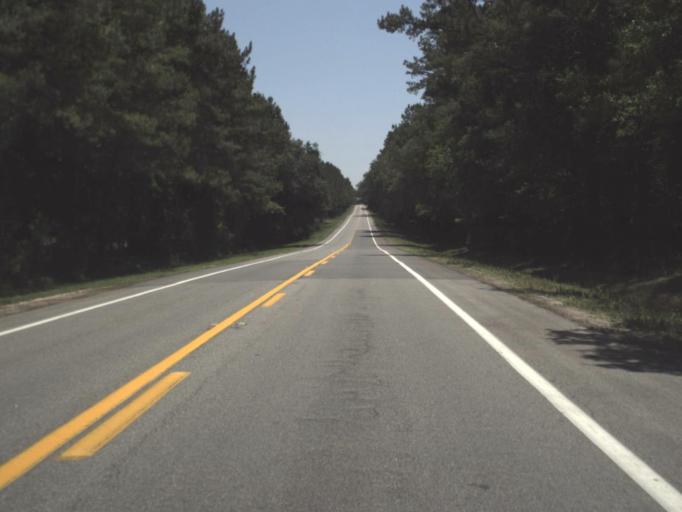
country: US
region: Florida
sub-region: Suwannee County
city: Live Oak
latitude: 30.3658
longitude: -83.1396
